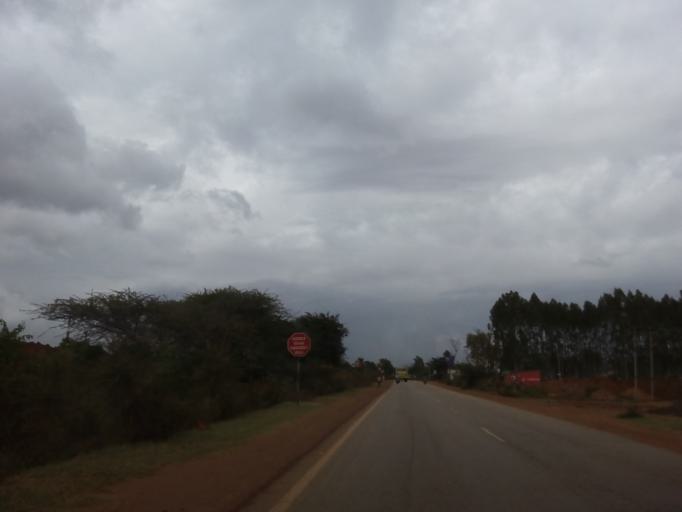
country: IN
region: Karnataka
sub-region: Davanagere
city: Harihar
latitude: 14.5329
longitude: 75.7692
